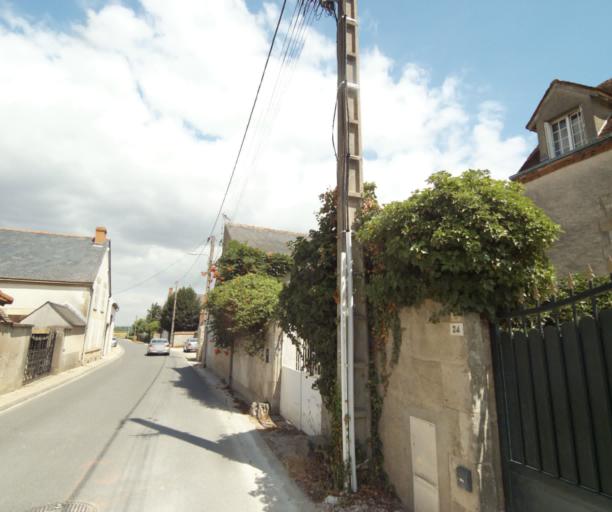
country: FR
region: Centre
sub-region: Departement du Loiret
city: Mardie
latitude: 47.8755
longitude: 2.0453
